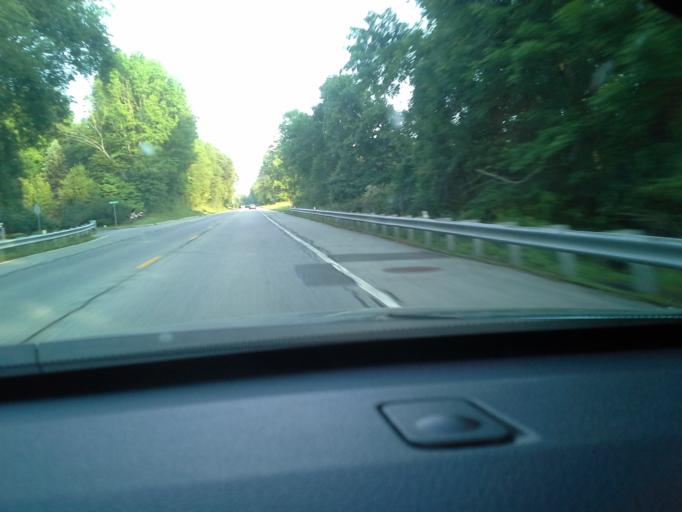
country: US
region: Maryland
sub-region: Calvert County
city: Owings
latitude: 38.7105
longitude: -76.5928
